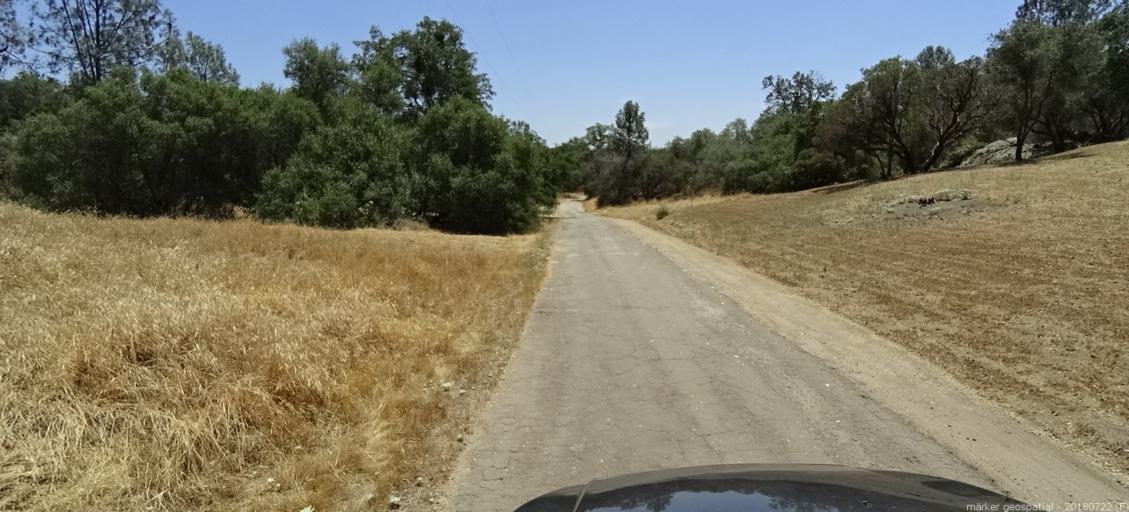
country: US
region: California
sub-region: Madera County
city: Coarsegold
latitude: 37.2392
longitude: -119.7330
